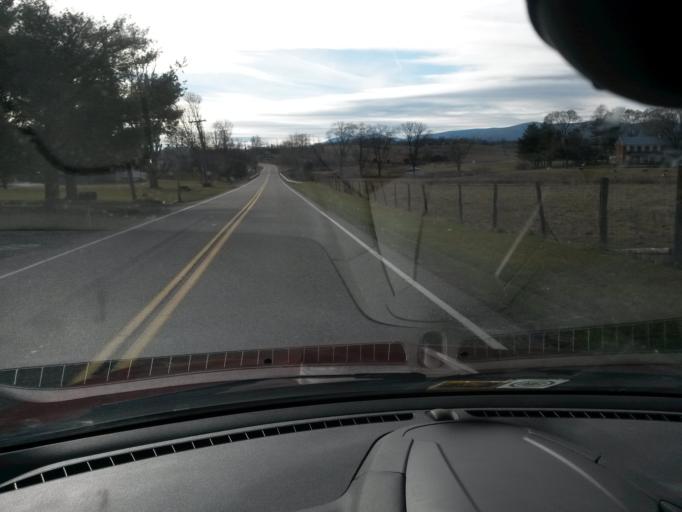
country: US
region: Virginia
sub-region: City of Staunton
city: Staunton
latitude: 38.2717
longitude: -79.1477
